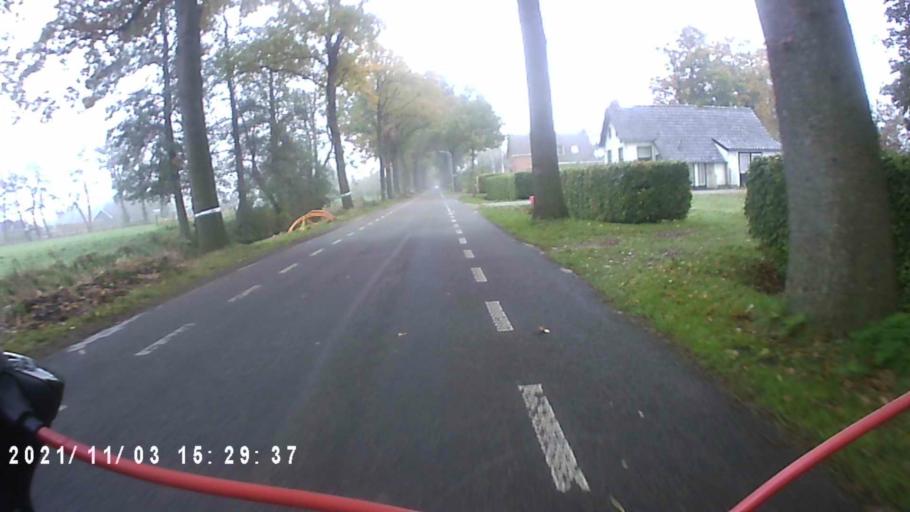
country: NL
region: Groningen
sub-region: Gemeente Leek
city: Leek
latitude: 53.1354
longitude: 6.3725
